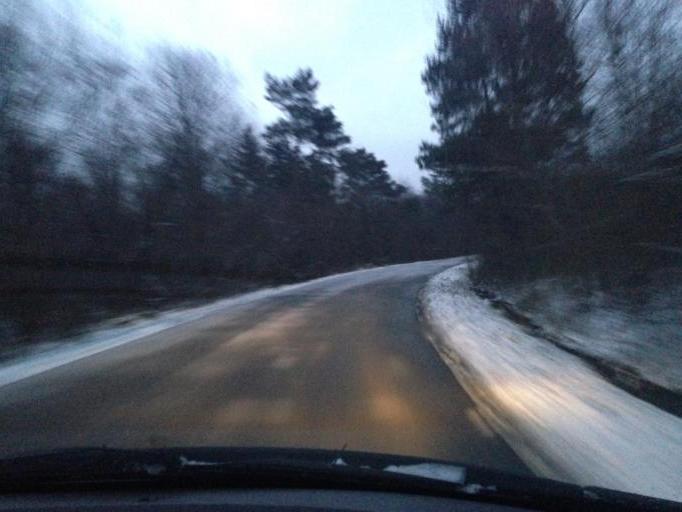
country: PL
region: Subcarpathian Voivodeship
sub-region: Powiat jasielski
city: Krempna
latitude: 49.5192
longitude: 21.5429
